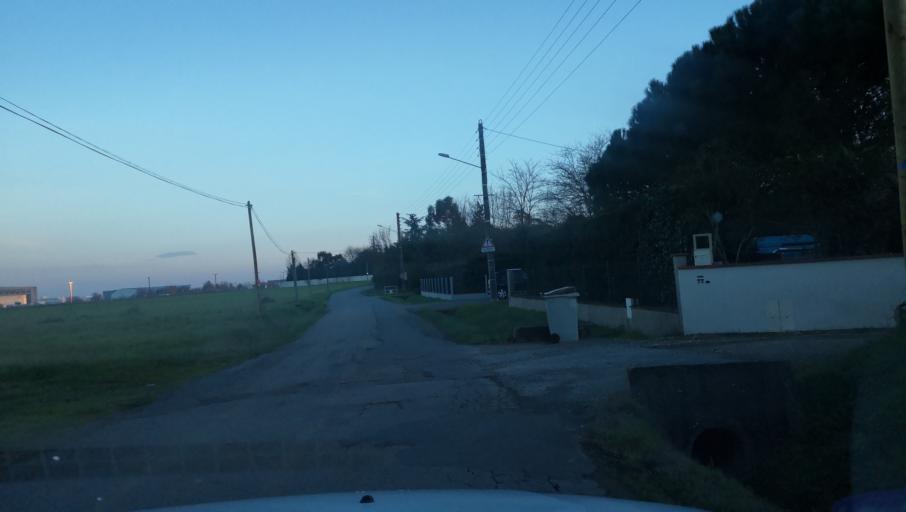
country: FR
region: Midi-Pyrenees
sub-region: Departement de la Haute-Garonne
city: Cornebarrieu
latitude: 43.6642
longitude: 1.3437
